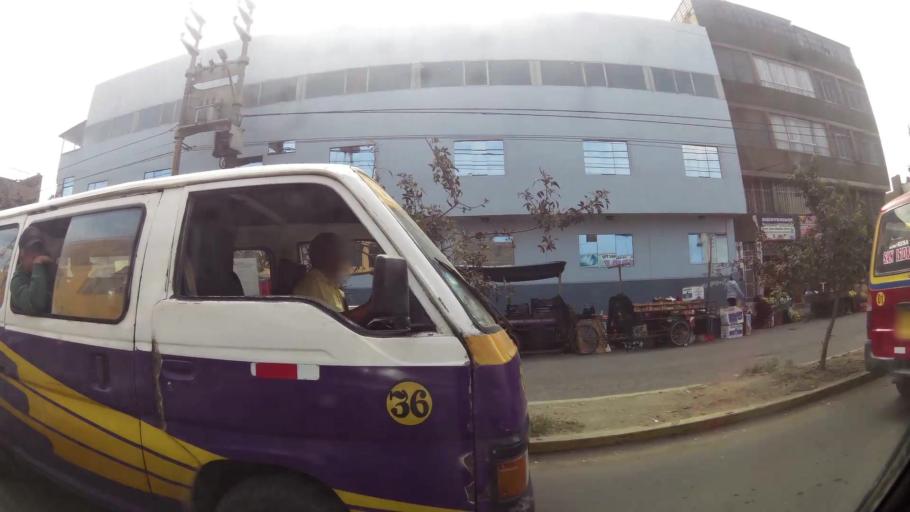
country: PE
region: La Libertad
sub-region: Provincia de Trujillo
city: Trujillo
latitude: -8.1131
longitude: -79.0201
